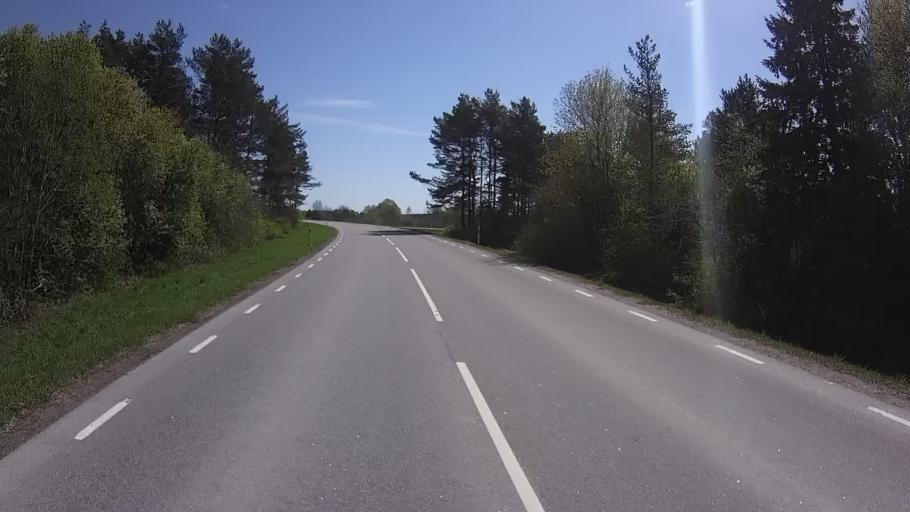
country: EE
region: Harju
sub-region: Keila linn
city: Keila
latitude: 59.2987
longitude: 24.3246
